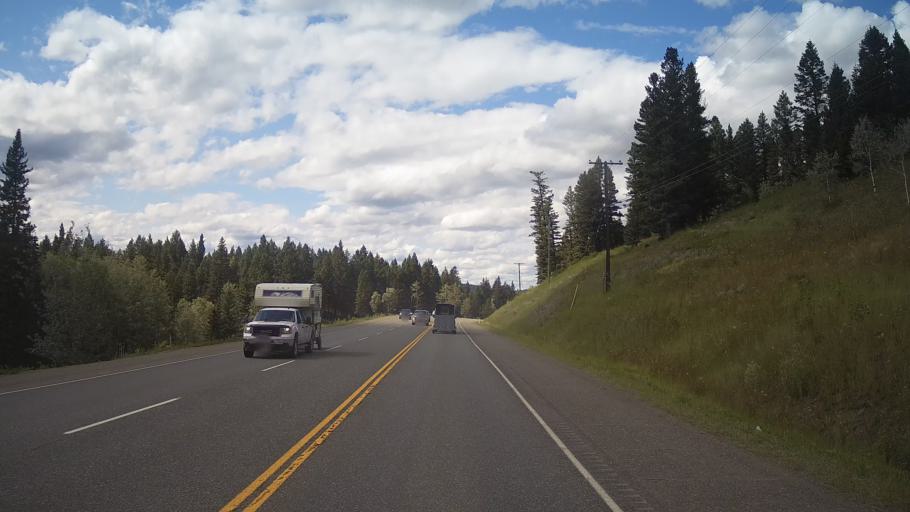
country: CA
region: British Columbia
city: Williams Lake
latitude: 51.7623
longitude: -121.3767
